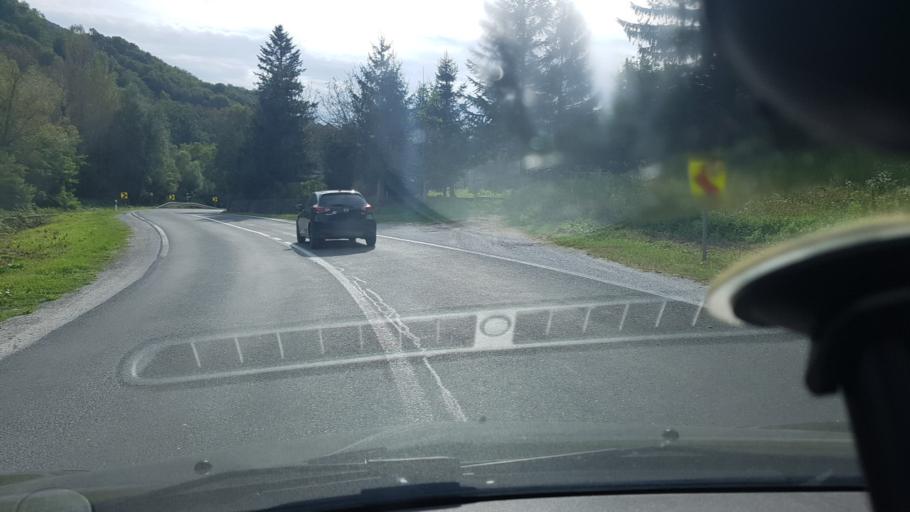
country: HR
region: Varazdinska
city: Lepoglava
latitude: 46.1987
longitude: 16.0029
